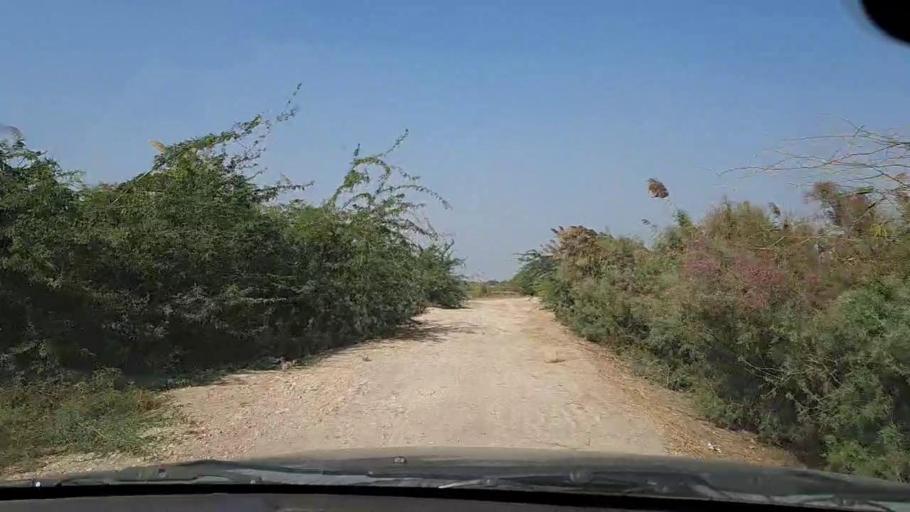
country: PK
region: Sindh
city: Chuhar Jamali
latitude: 24.4370
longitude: 67.7992
